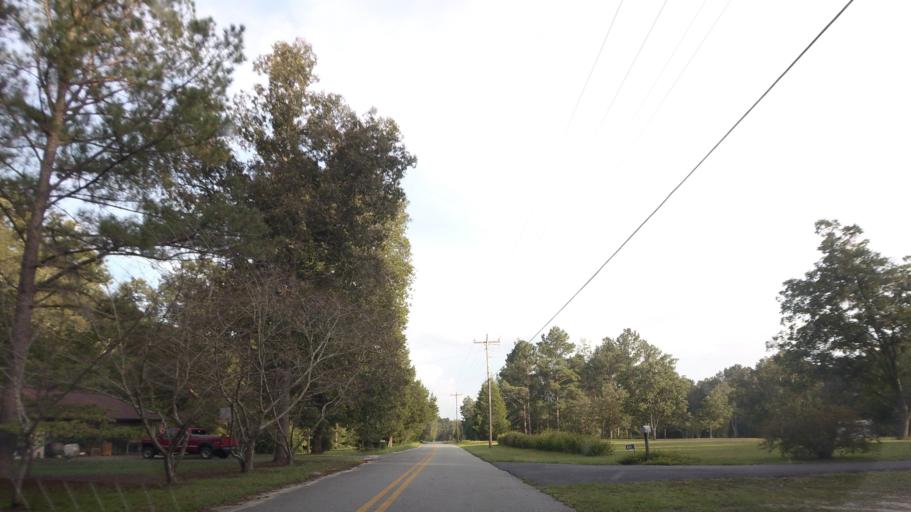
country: US
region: Georgia
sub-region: Wilkinson County
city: Gordon
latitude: 32.8338
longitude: -83.3940
